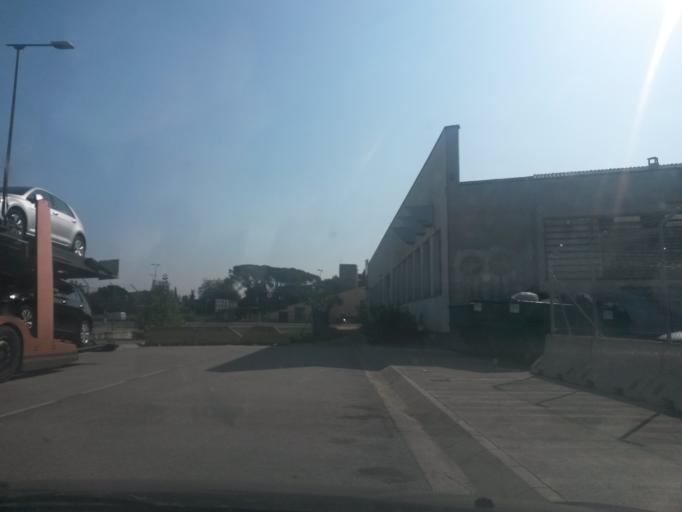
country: ES
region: Catalonia
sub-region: Provincia de Girona
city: Fornells de la Selva
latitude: 41.9371
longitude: 2.7984
